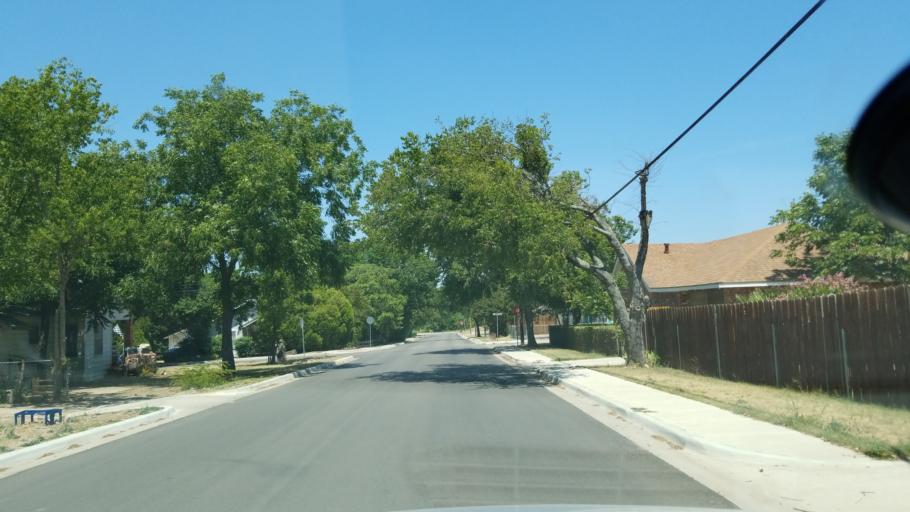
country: US
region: Texas
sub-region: Dallas County
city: Cockrell Hill
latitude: 32.7370
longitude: -96.8841
